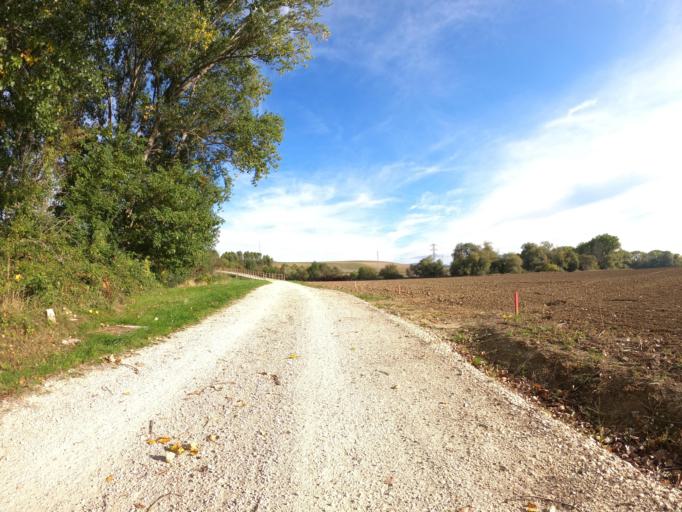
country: ES
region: Navarre
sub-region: Provincia de Navarra
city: Orkoien
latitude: 42.8160
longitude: -1.7395
